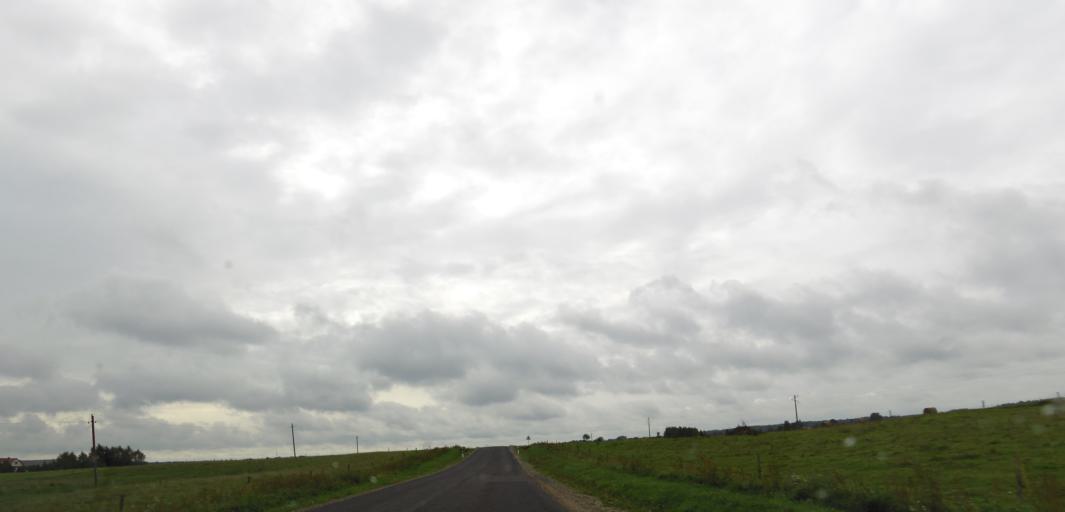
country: LT
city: Moletai
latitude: 55.2682
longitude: 25.3544
